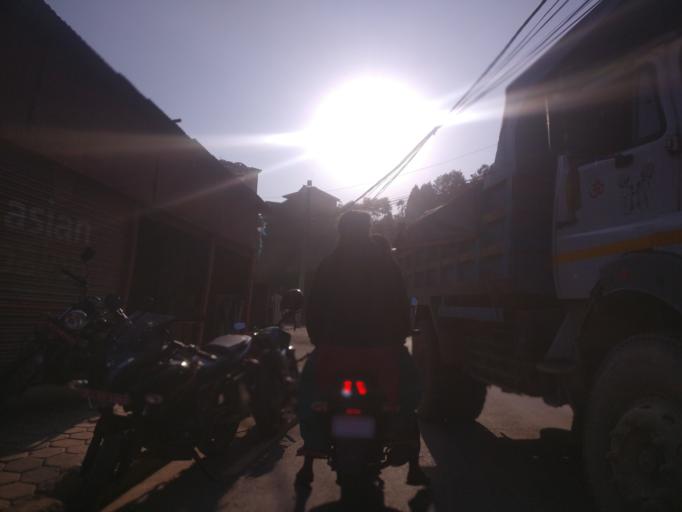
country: NP
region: Central Region
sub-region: Bagmati Zone
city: Patan
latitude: 27.6516
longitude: 85.3307
